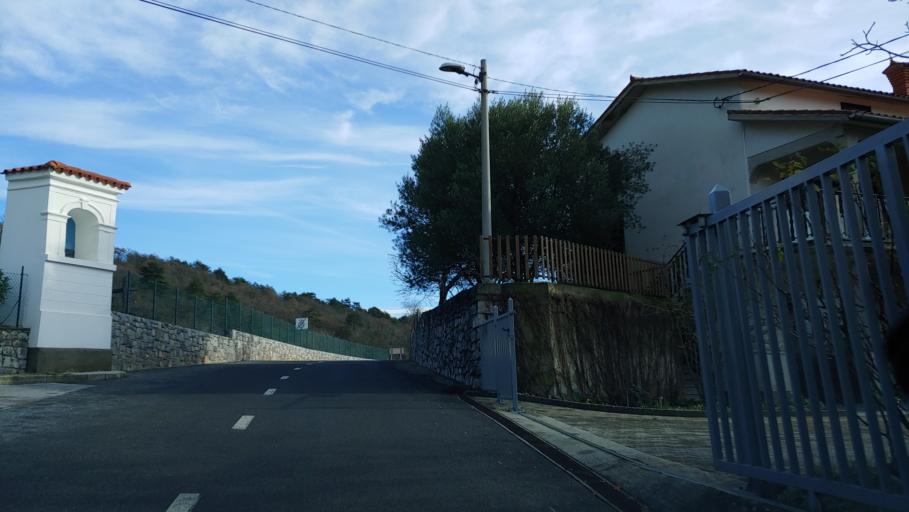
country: SI
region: Komen
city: Komen
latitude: 45.8108
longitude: 13.6942
